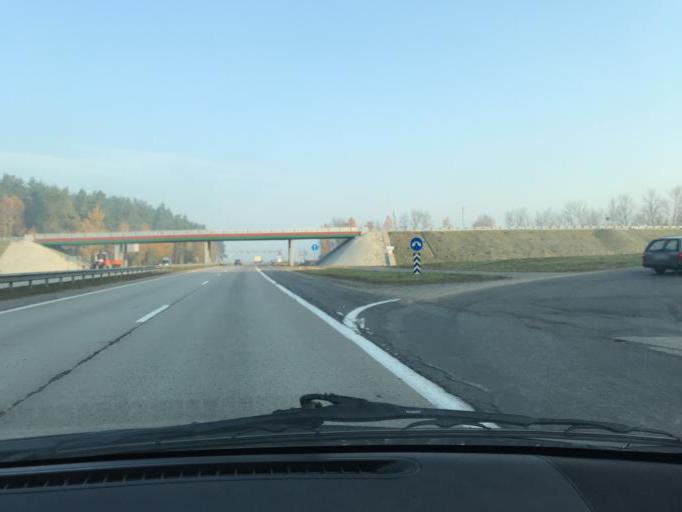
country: BY
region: Minsk
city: Borovlyany
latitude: 54.0024
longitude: 27.6572
